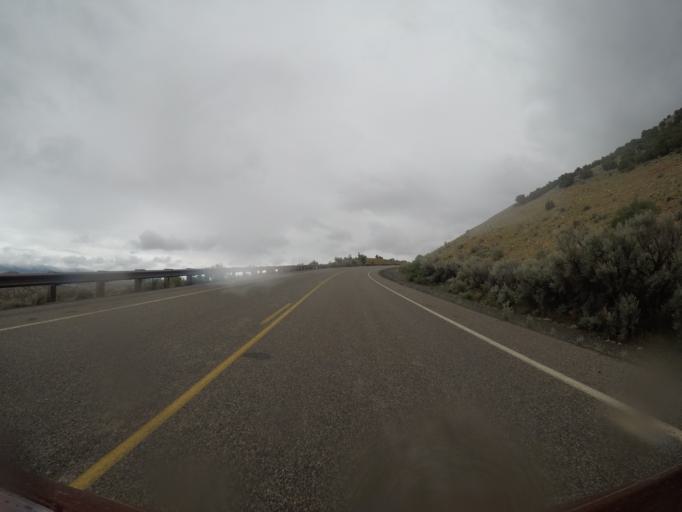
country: US
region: Wyoming
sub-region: Big Horn County
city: Lovell
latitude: 45.0770
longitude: -108.2585
